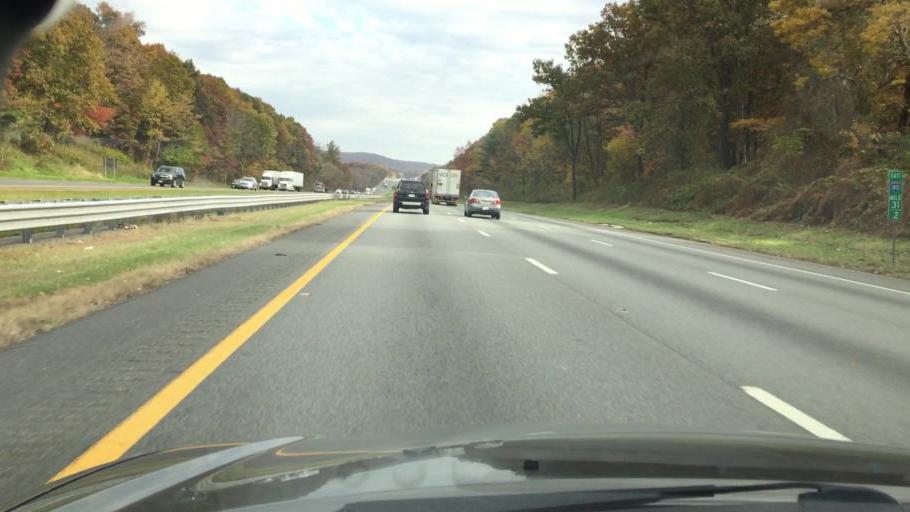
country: US
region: New Jersey
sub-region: Morris County
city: Kenvil
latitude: 40.9006
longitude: -74.6239
